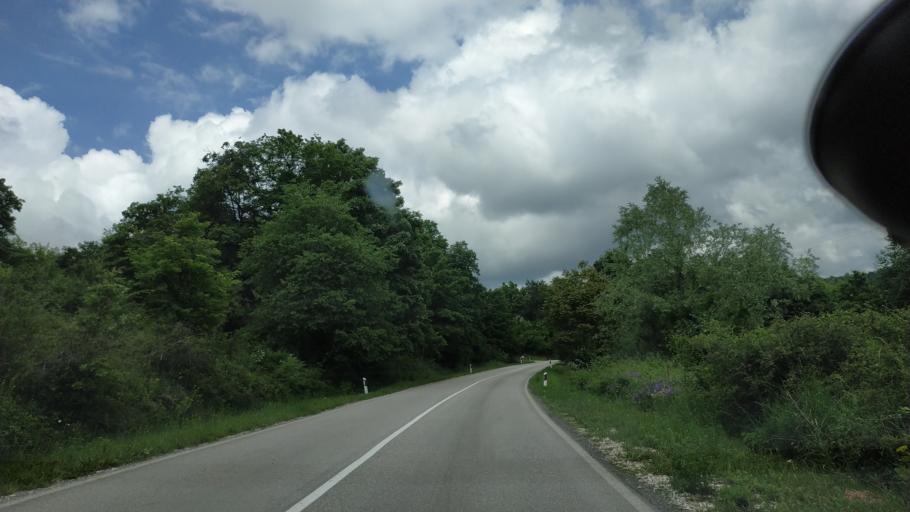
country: RS
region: Central Serbia
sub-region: Borski Okrug
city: Bor
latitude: 44.0638
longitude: 22.0374
